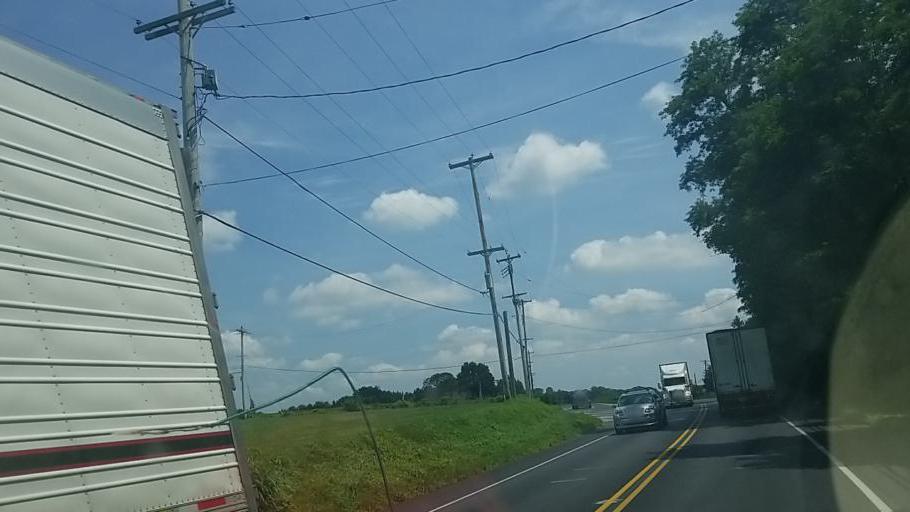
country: US
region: Pennsylvania
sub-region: Chester County
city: Toughkenamon
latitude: 39.8018
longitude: -75.7382
